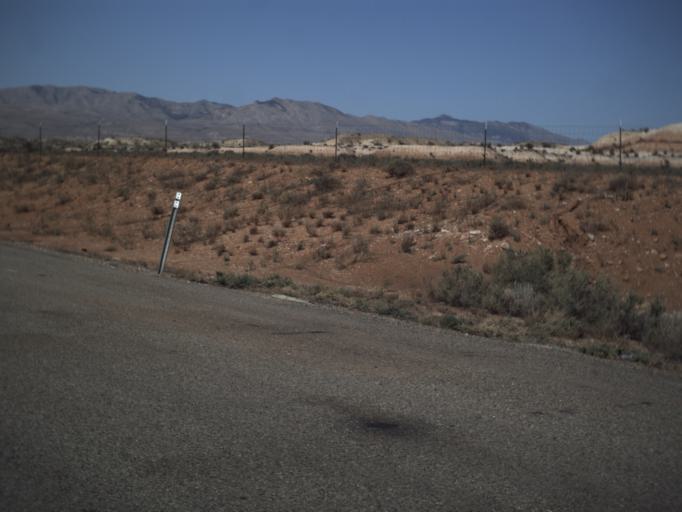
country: US
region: Utah
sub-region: Washington County
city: Saint George
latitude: 37.0011
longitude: -113.5609
